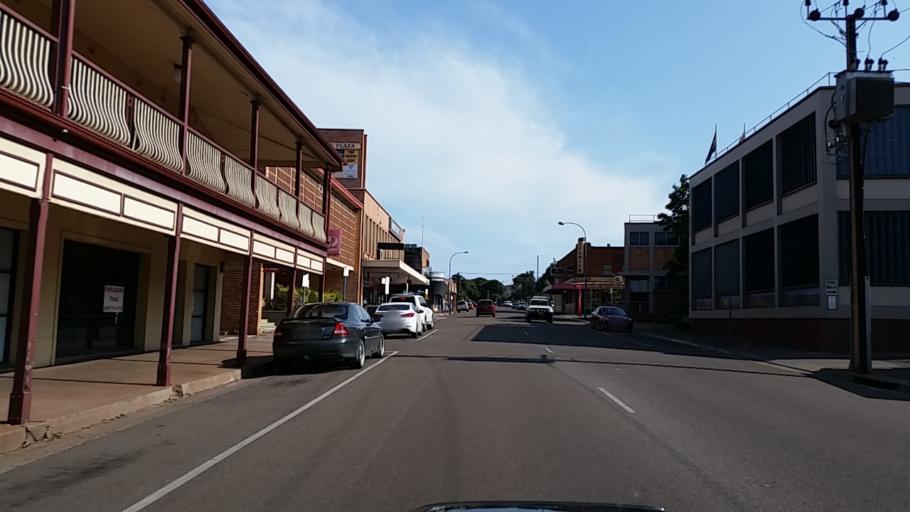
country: AU
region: South Australia
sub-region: Whyalla
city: Whyalla
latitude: -33.0341
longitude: 137.5860
